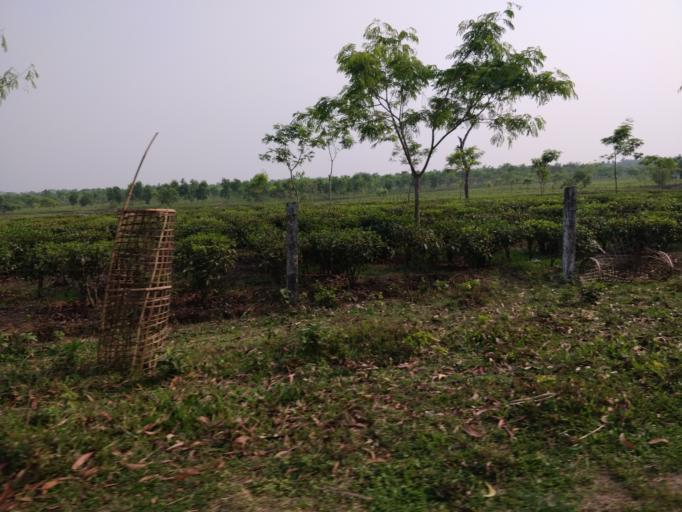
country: IN
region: Tripura
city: Khowai
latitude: 24.1294
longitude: 91.3817
